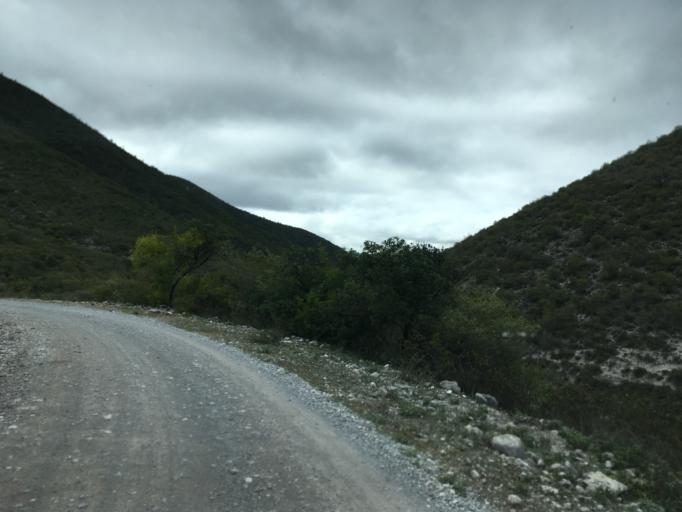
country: MX
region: Hidalgo
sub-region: Metztitlan
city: Fontezuelas
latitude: 20.6237
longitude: -98.8654
